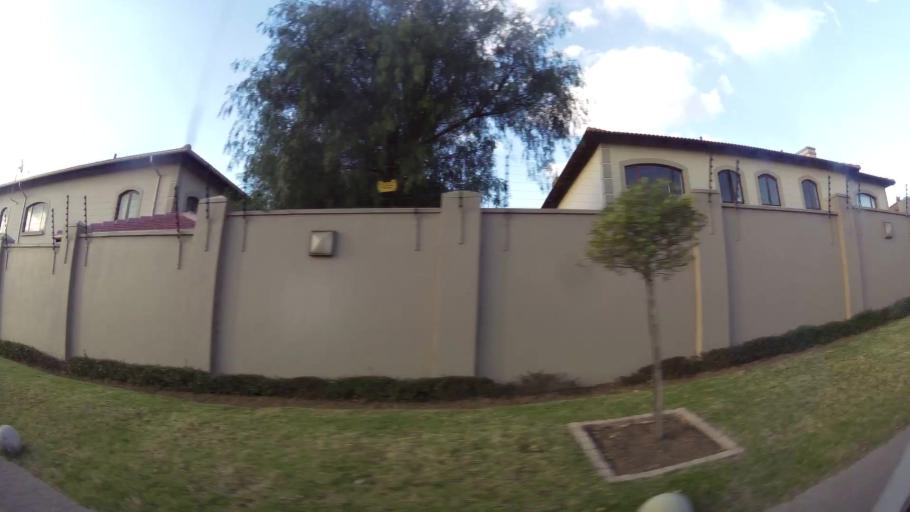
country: ZA
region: Gauteng
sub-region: City of Johannesburg Metropolitan Municipality
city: Diepsloot
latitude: -25.9964
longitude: 28.0007
